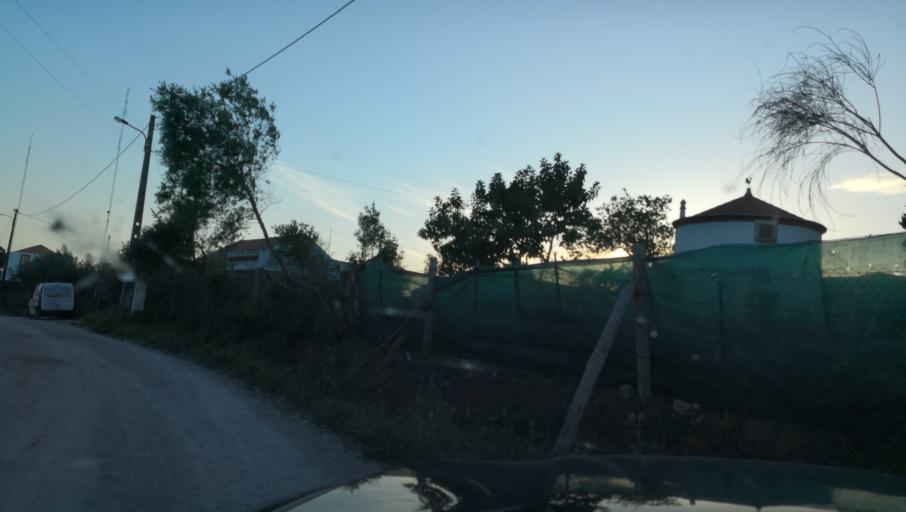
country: PT
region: Setubal
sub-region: Setubal
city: Setubal
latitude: 38.5248
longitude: -8.9162
